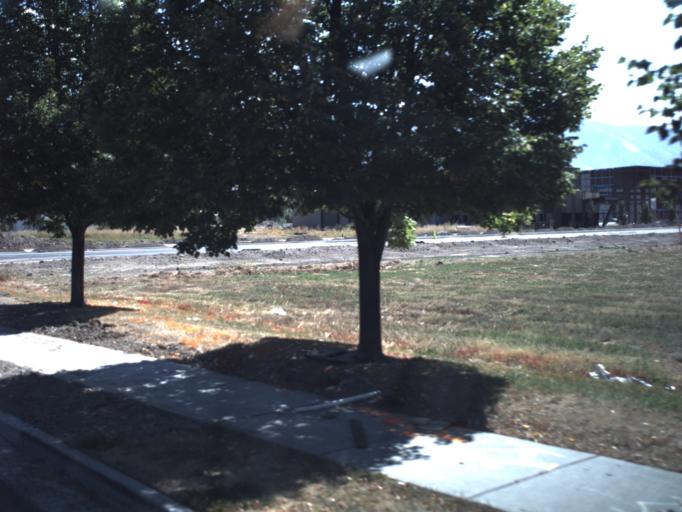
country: US
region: Utah
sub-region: Cache County
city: Hyde Park
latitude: 41.7777
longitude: -111.8312
